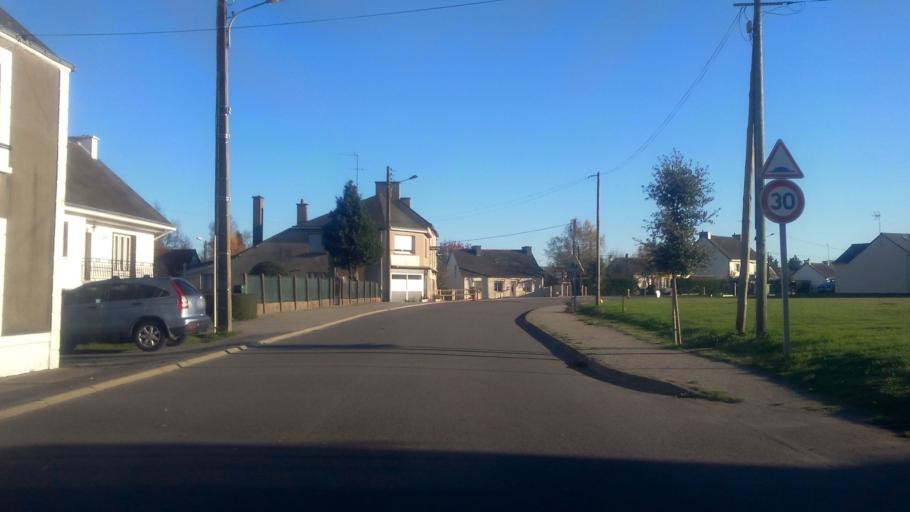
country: FR
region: Brittany
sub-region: Departement du Morbihan
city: Peillac
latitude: 47.7159
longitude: -2.2232
